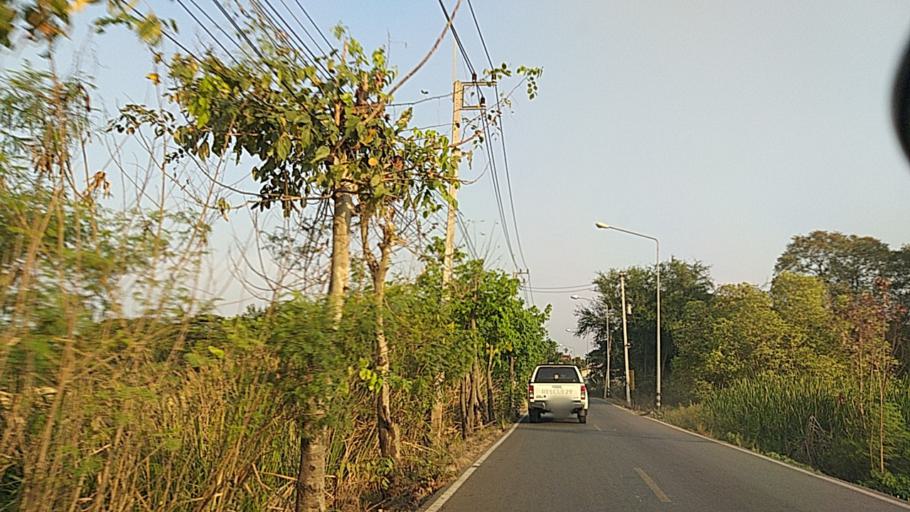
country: TH
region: Sara Buri
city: Nong Khae
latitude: 14.2771
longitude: 100.8208
